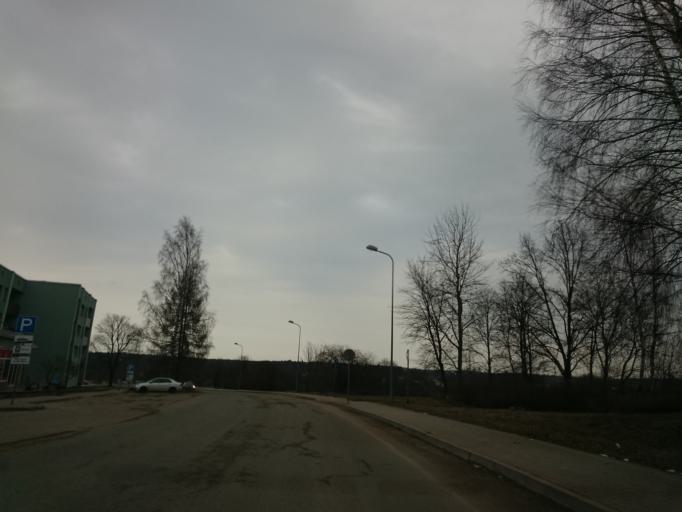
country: LV
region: Cesu Rajons
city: Cesis
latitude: 57.3159
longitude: 25.2594
